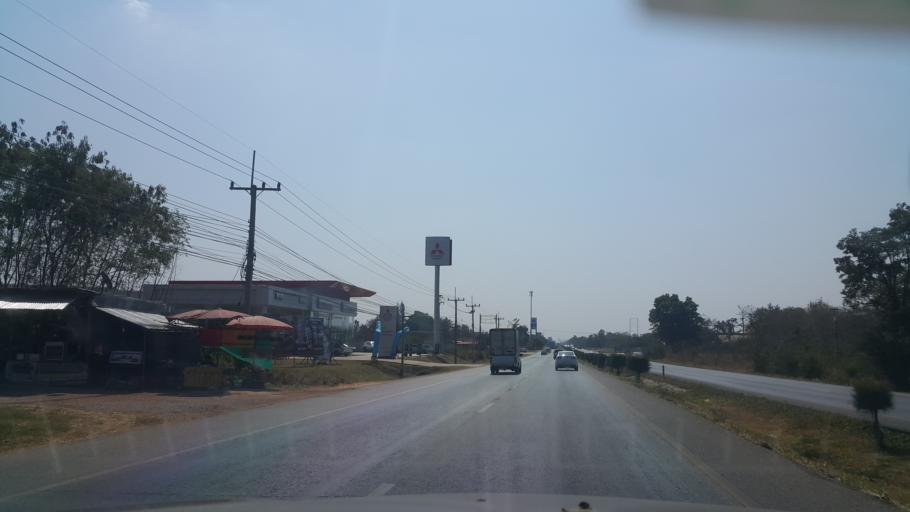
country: TH
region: Khon Kaen
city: Ban Phai
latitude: 16.0282
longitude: 102.7103
